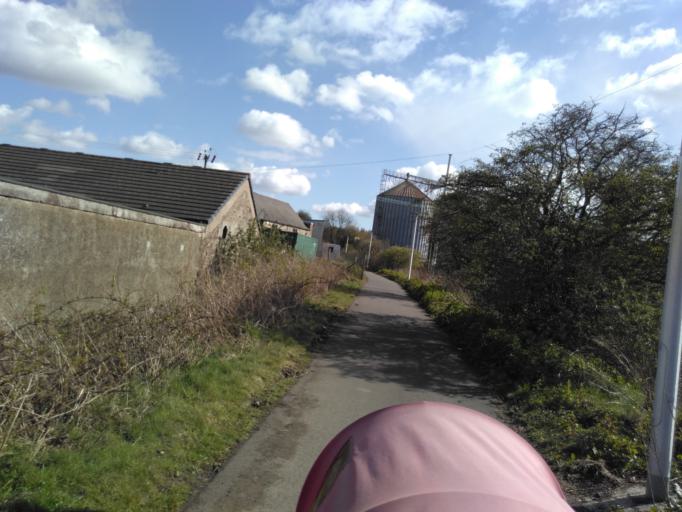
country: GB
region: Scotland
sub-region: Midlothian
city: Loanhead
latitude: 55.8869
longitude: -3.1474
